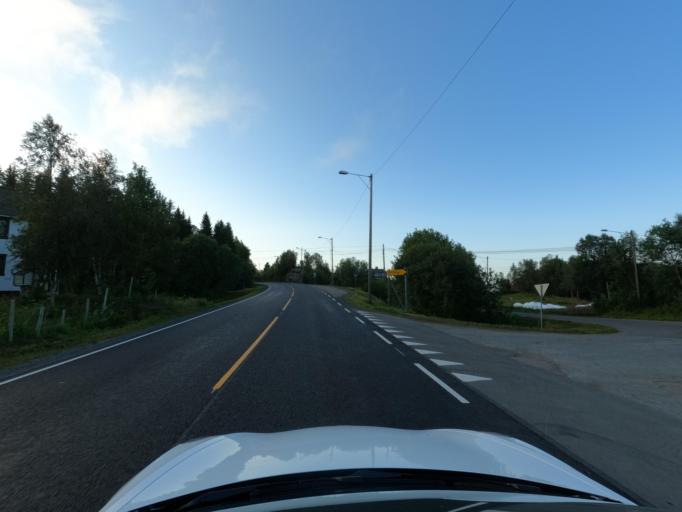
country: NO
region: Troms
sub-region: Skanland
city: Evenskjer
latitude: 68.6685
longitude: 16.5758
